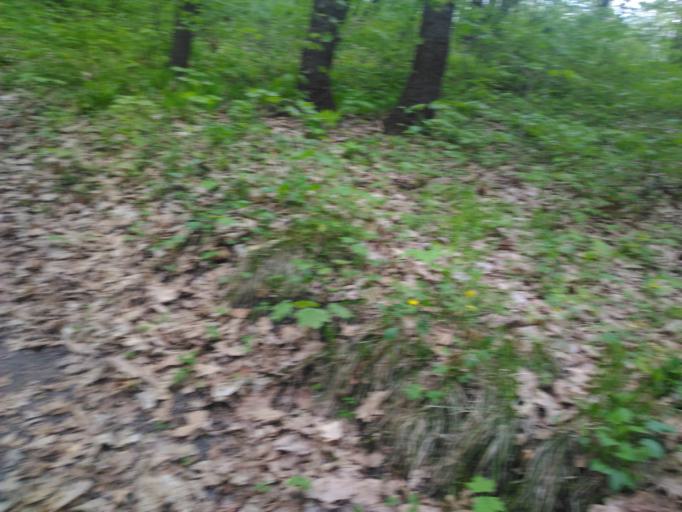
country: RU
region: Ulyanovsk
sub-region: Ulyanovskiy Rayon
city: Ulyanovsk
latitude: 54.2718
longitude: 48.3499
